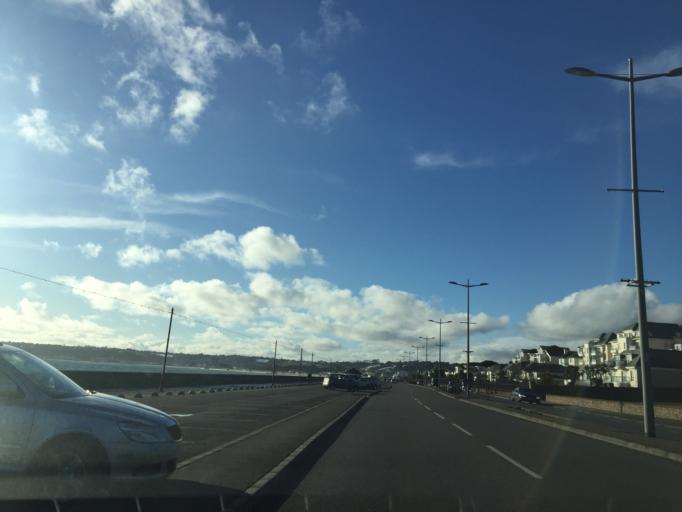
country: JE
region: St Helier
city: Saint Helier
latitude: 49.1902
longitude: -2.1212
